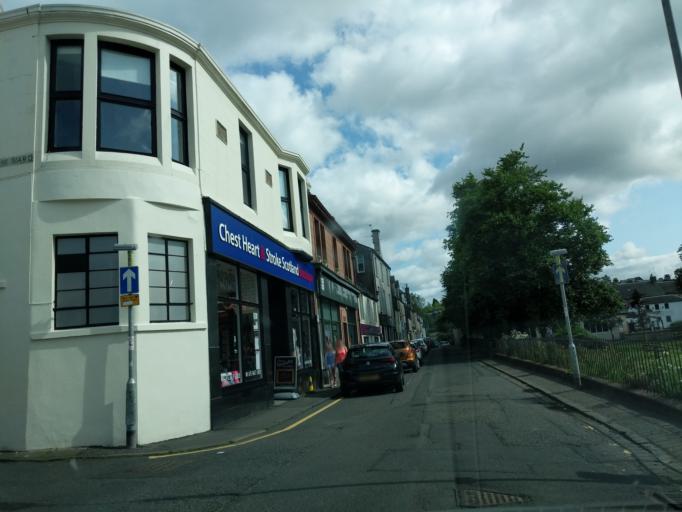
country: GB
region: Scotland
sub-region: South Lanarkshire
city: Strathaven
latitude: 55.6779
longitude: -4.0652
